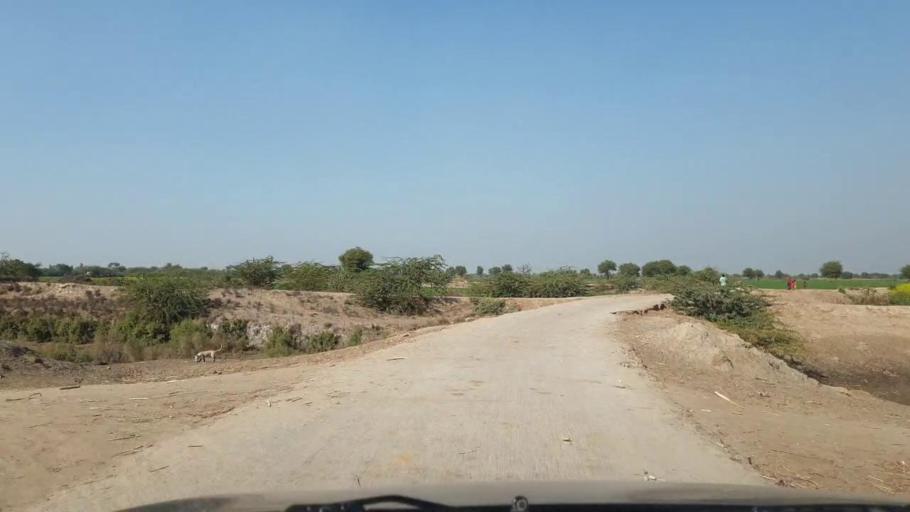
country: PK
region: Sindh
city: Jhol
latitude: 25.9090
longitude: 68.8273
